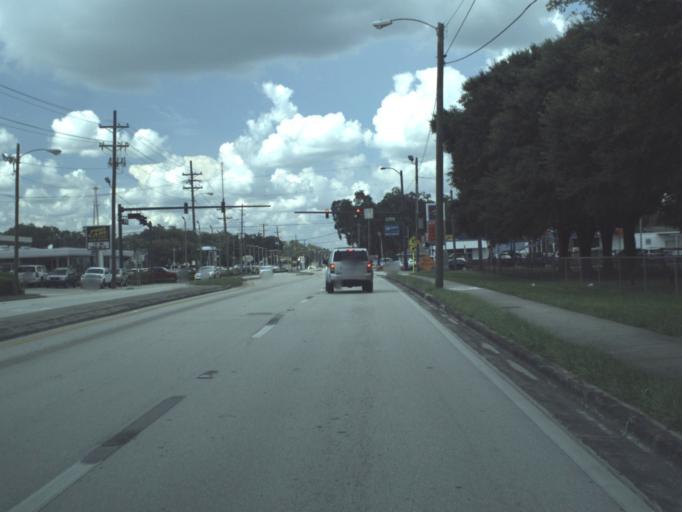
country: US
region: Florida
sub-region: Polk County
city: Lakeland
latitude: 28.0396
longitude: -81.9406
